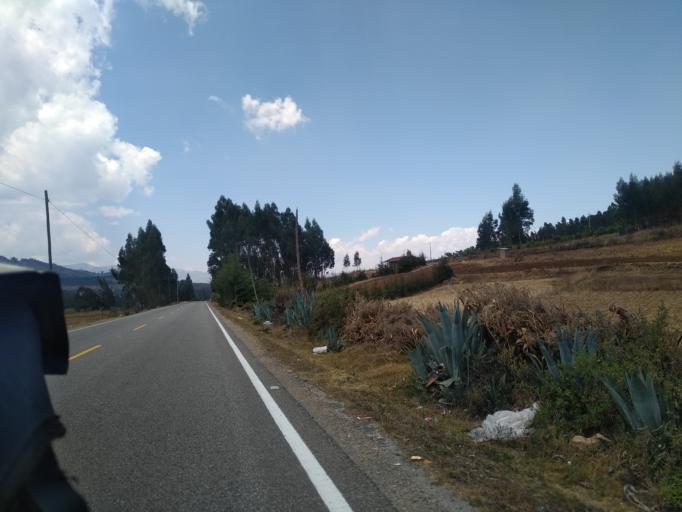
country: PE
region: Cajamarca
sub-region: San Marcos
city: San Marcos
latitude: -7.2802
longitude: -78.2331
